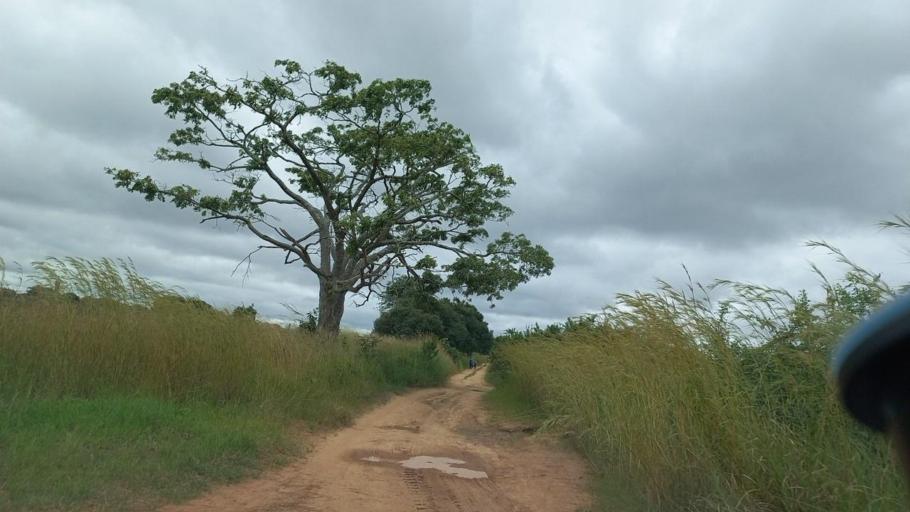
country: ZM
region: Lusaka
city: Lusaka
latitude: -15.1241
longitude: 28.3712
